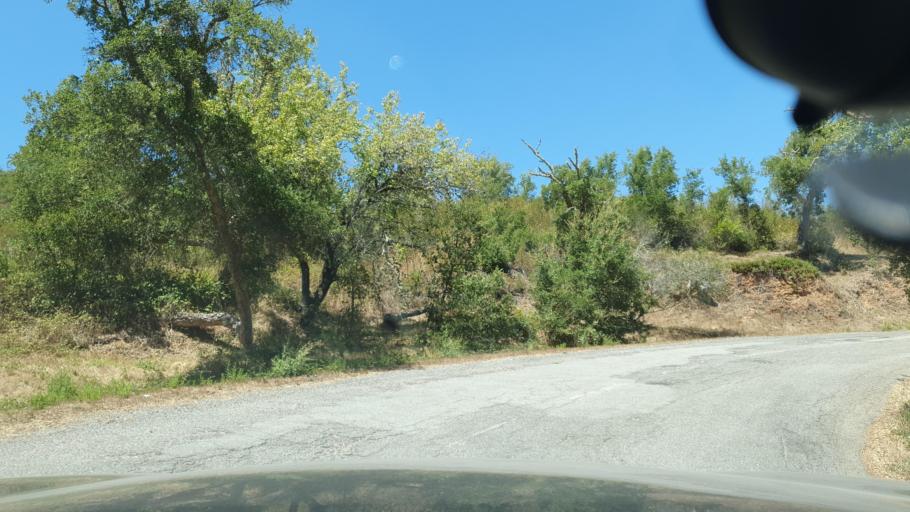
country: PT
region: Beja
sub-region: Odemira
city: Odemira
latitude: 37.6045
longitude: -8.4951
